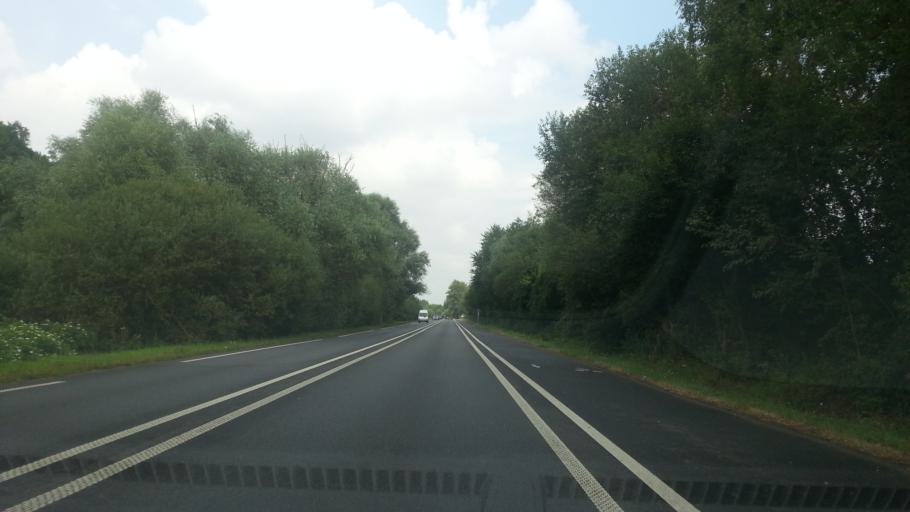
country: FR
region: Picardie
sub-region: Departement de l'Oise
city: Saint-Maximin
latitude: 49.2295
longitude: 2.4330
